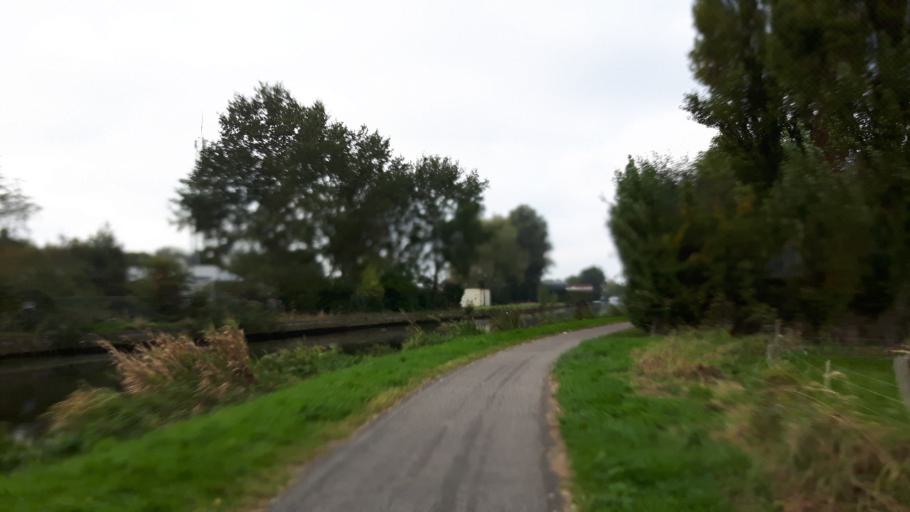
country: NL
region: South Holland
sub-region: Gemeente Vlist
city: Haastrecht
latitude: 52.0029
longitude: 4.7845
